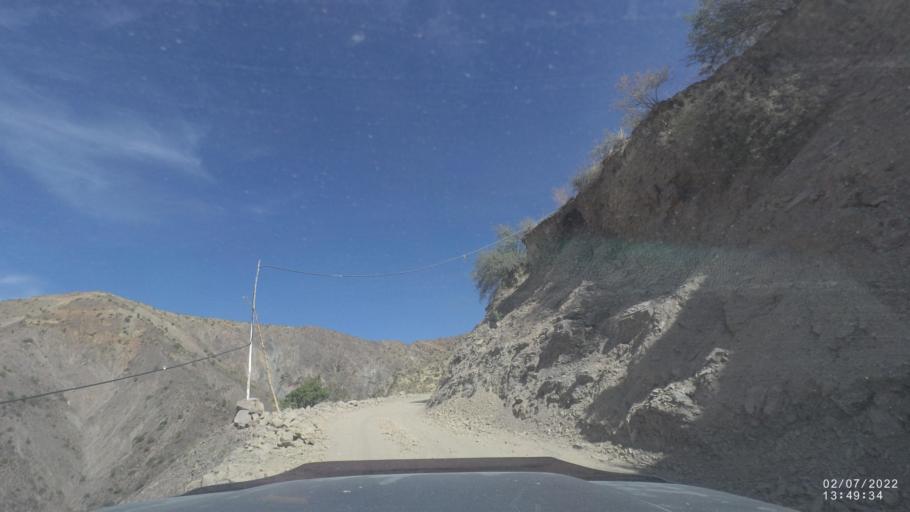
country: BO
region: Cochabamba
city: Irpa Irpa
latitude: -17.8212
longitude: -66.3751
